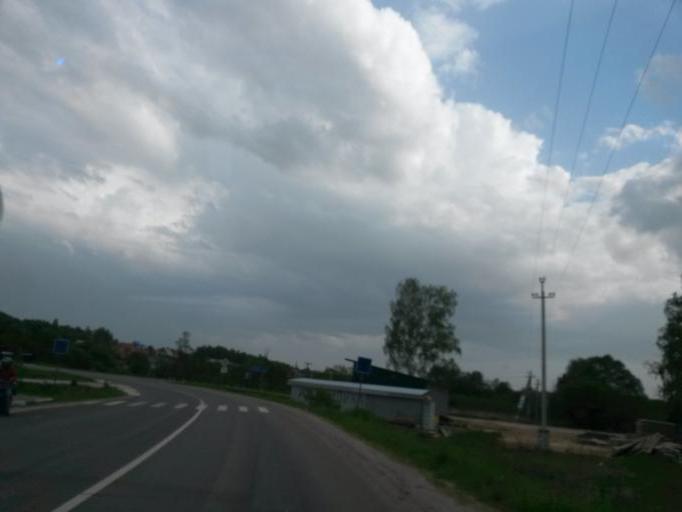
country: RU
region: Moskovskaya
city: Lyubuchany
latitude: 55.2772
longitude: 37.6188
